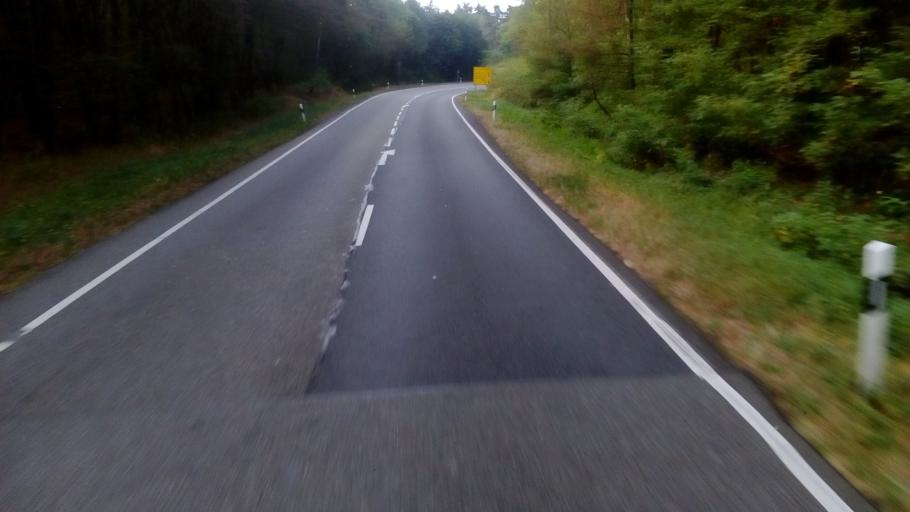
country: DE
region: Rheinland-Pfalz
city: Berg
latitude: 48.9993
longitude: 8.1808
